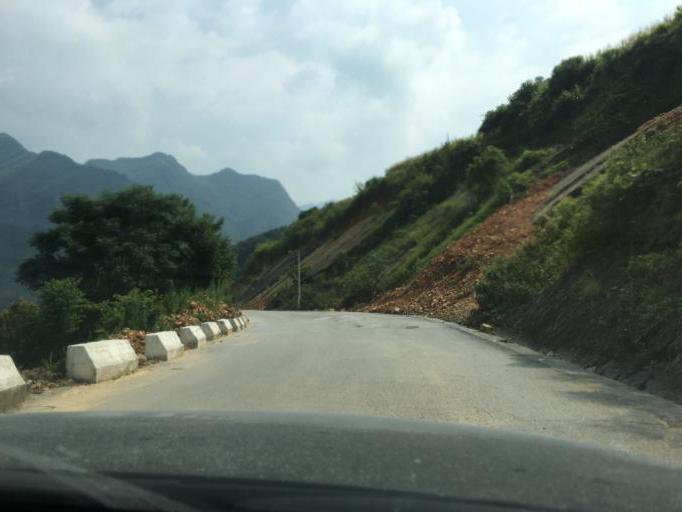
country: CN
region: Guangxi Zhuangzu Zizhiqu
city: Tongle
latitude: 25.2982
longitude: 106.2676
